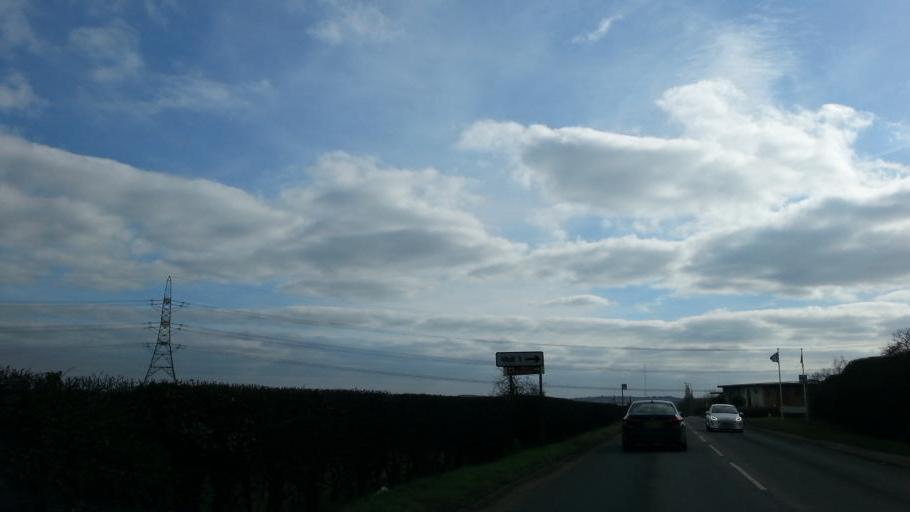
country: GB
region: England
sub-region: Staffordshire
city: Shenstone
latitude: 52.6566
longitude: -1.8342
